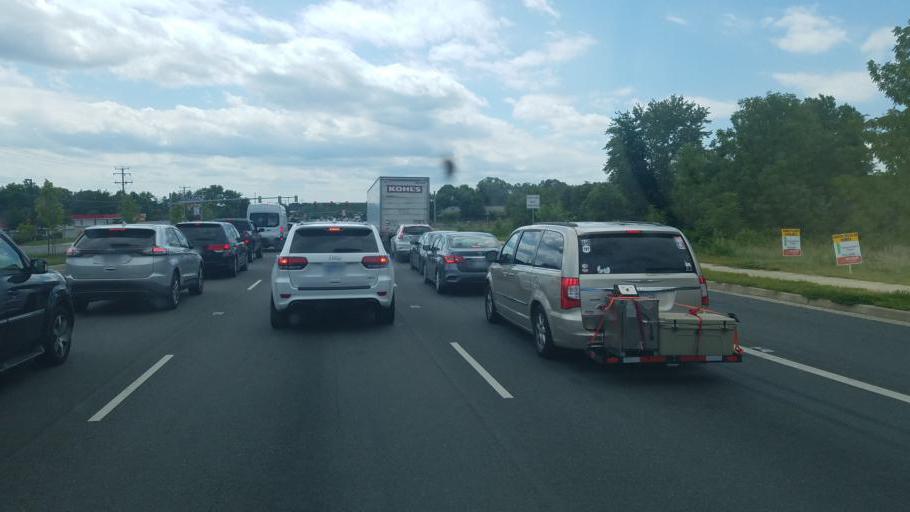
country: US
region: Virginia
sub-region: Stafford County
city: Falmouth
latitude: 38.3485
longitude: -77.5023
